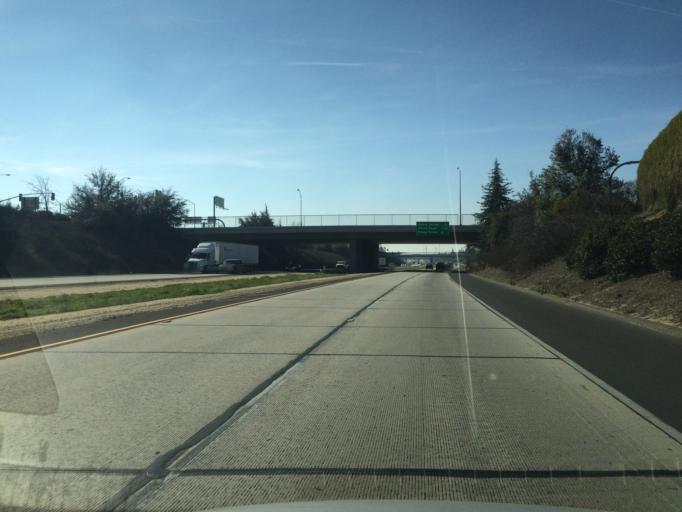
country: US
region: California
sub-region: Tulare County
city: Visalia
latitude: 36.3272
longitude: -119.3301
